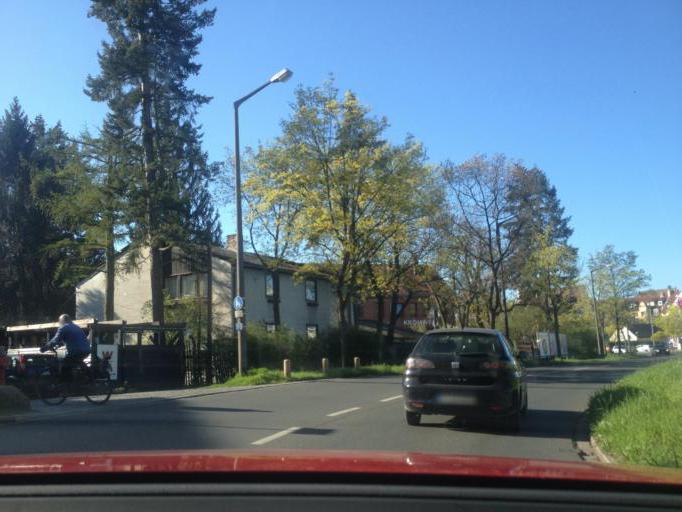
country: DE
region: Bavaria
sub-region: Regierungsbezirk Mittelfranken
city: Nuernberg
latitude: 49.4666
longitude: 11.1280
